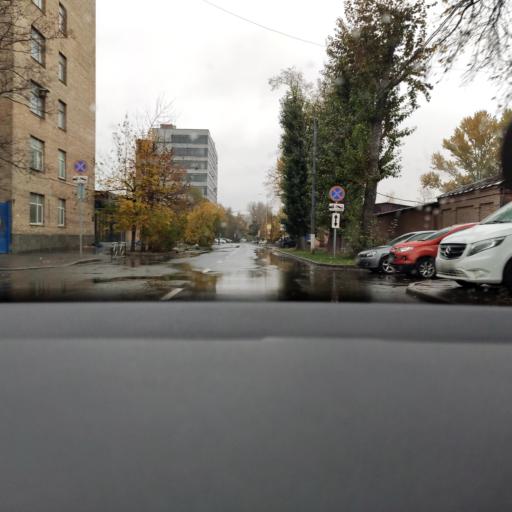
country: RU
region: Moscow
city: Ryazanskiy
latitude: 55.7504
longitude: 37.7700
